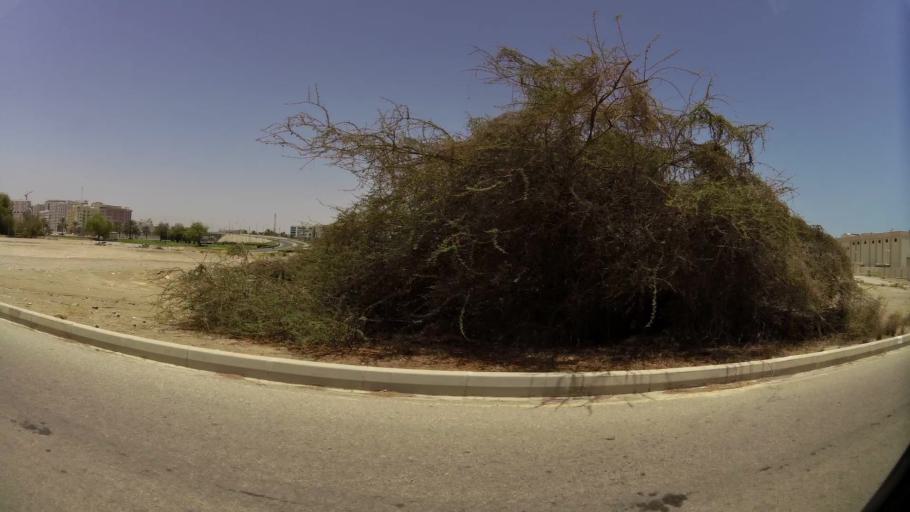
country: OM
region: Muhafazat Masqat
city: Bawshar
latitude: 23.5985
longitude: 58.4156
